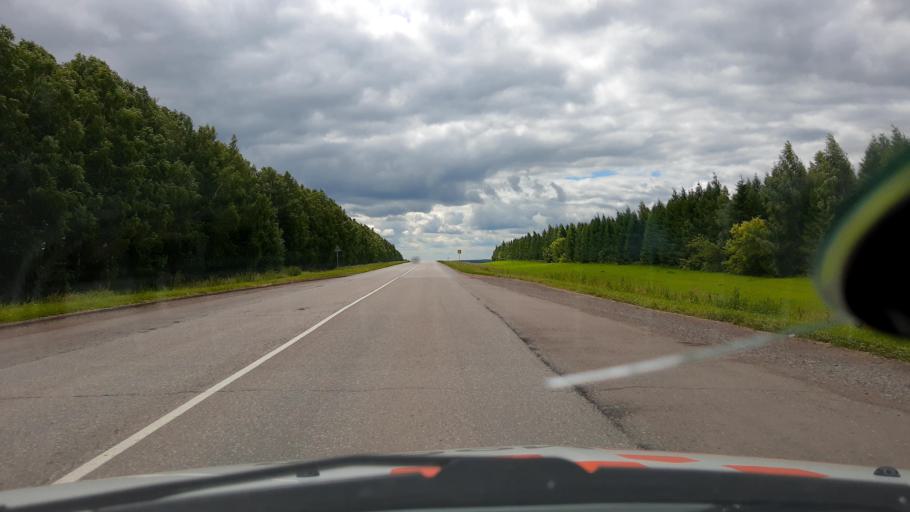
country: RU
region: Bashkortostan
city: Buzdyak
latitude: 54.7081
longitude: 54.5660
